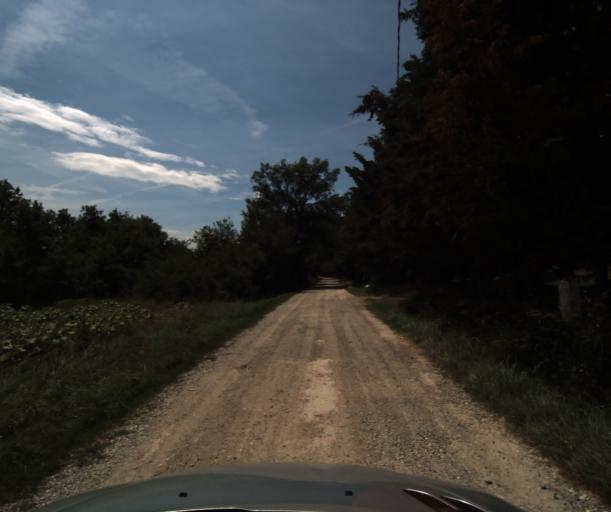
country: FR
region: Midi-Pyrenees
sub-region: Departement de la Haute-Garonne
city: Lherm
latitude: 43.4407
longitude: 1.2336
